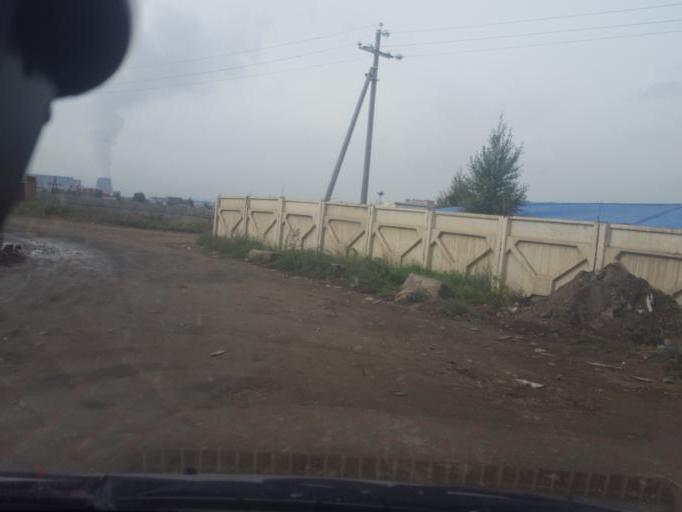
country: MN
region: Ulaanbaatar
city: Ulaanbaatar
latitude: 47.9158
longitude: 106.8005
